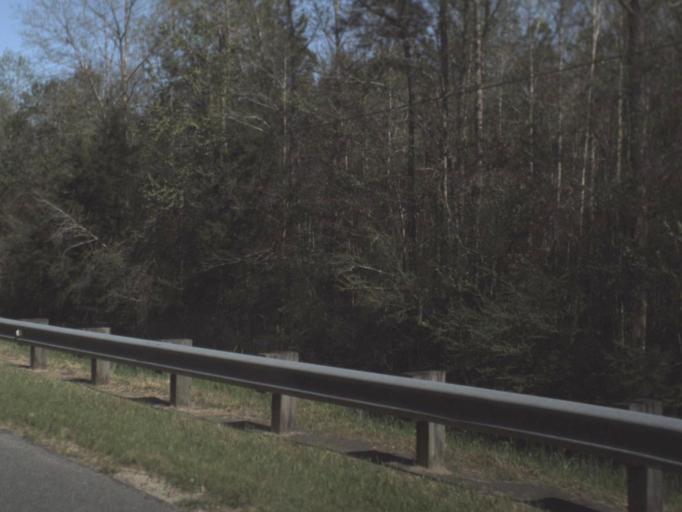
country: US
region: Florida
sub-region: Walton County
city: DeFuniak Springs
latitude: 30.7242
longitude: -85.9414
